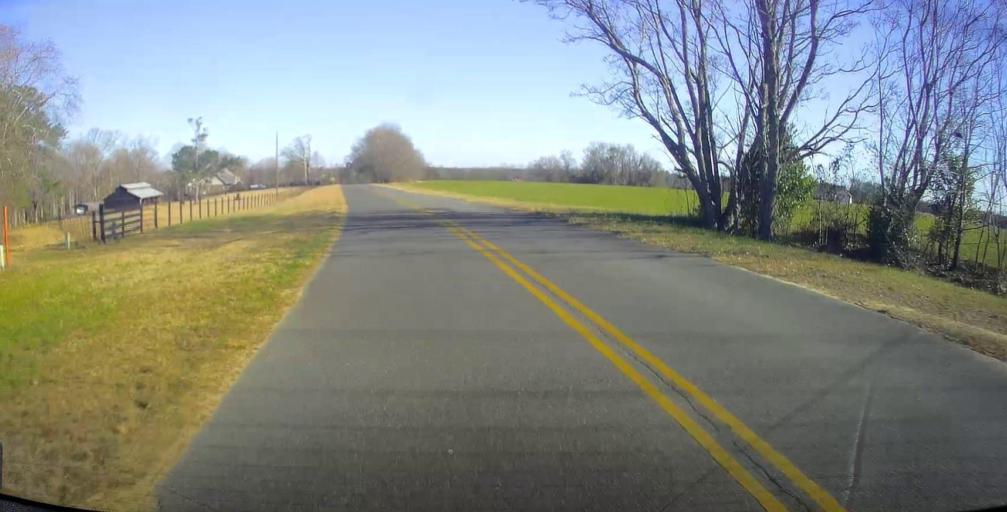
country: US
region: Georgia
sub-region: Taylor County
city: Butler
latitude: 32.6547
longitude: -84.3240
